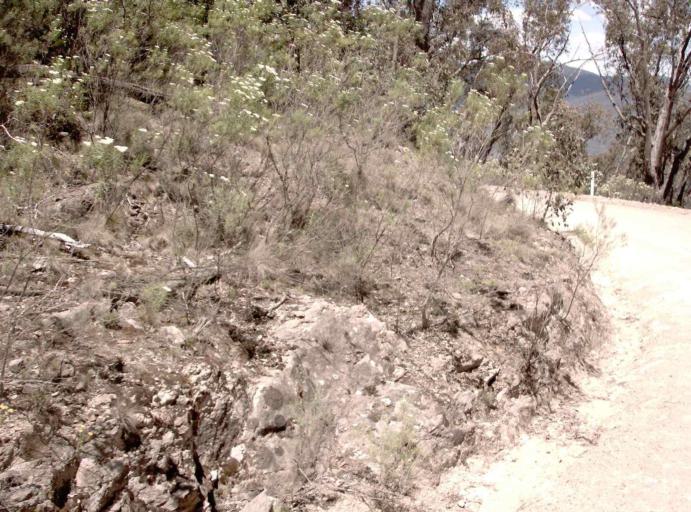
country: AU
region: New South Wales
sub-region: Snowy River
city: Jindabyne
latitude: -37.0883
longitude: 148.3272
